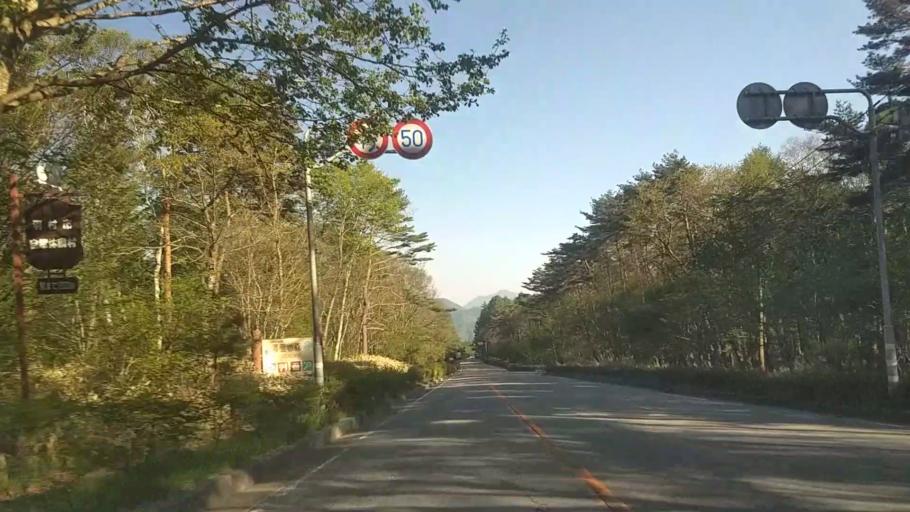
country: JP
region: Yamanashi
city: Nirasaki
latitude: 35.9279
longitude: 138.4300
